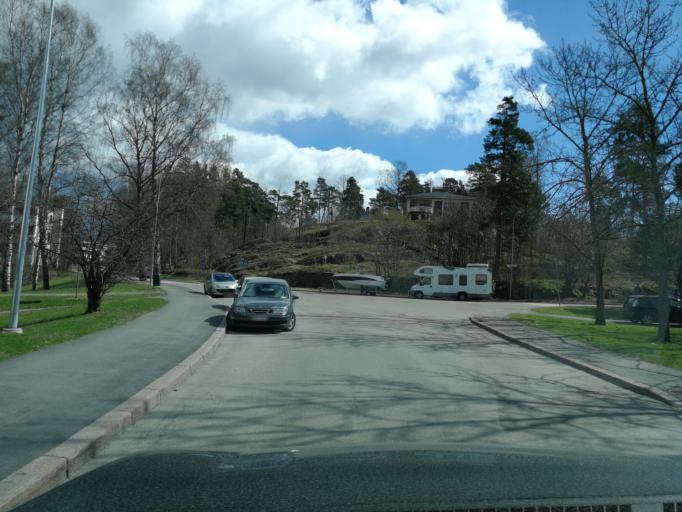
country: FI
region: Uusimaa
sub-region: Helsinki
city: Teekkarikylae
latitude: 60.1635
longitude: 24.8791
